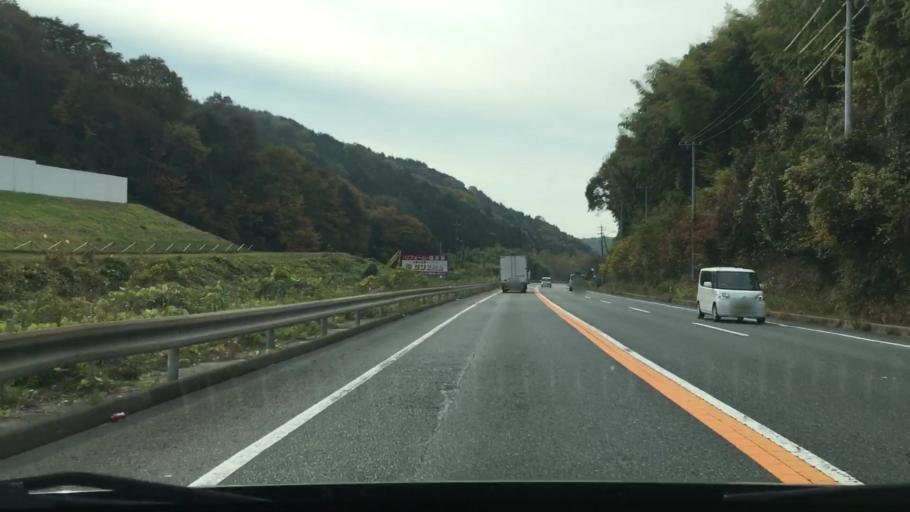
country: JP
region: Yamaguchi
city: Hikari
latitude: 34.0705
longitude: 131.9846
